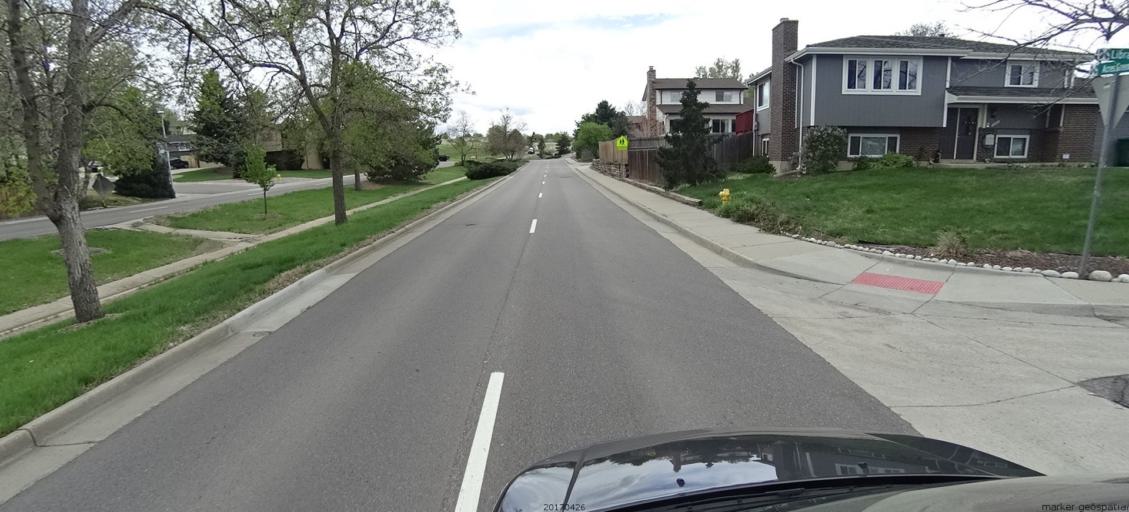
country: US
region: Colorado
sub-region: Douglas County
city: Acres Green
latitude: 39.5607
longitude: -104.8968
